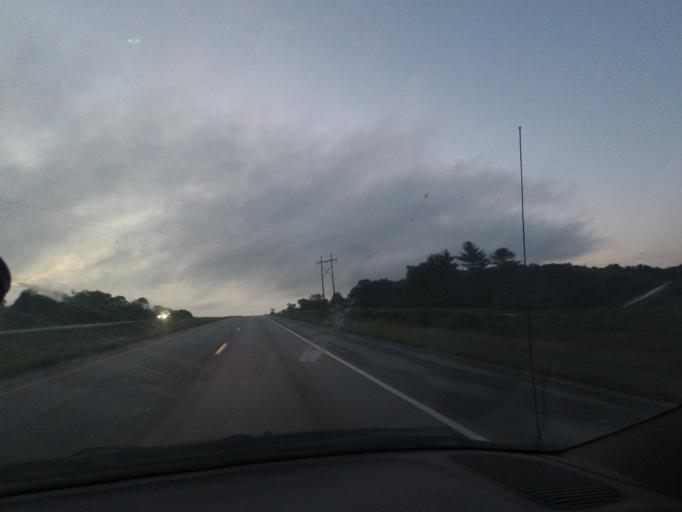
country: US
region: Missouri
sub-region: Linn County
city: Brookfield
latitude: 39.7633
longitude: -93.0282
